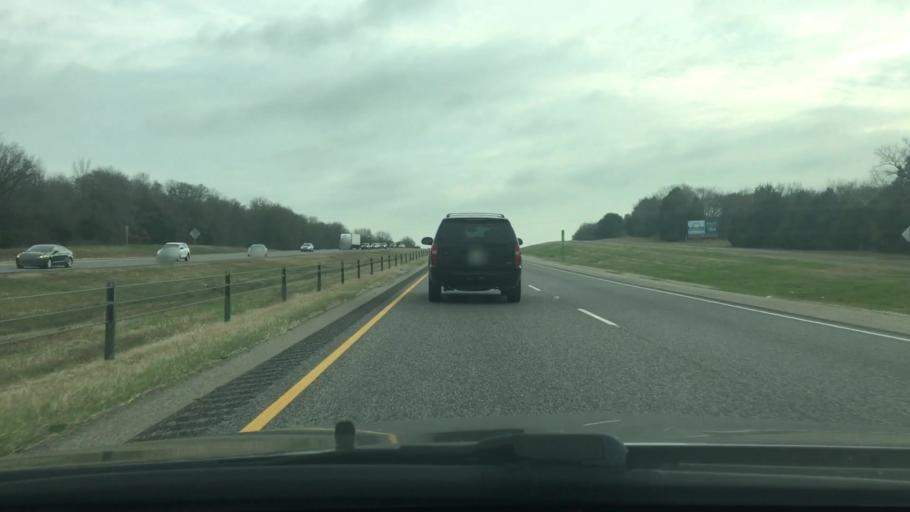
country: US
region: Texas
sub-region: Freestone County
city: Fairfield
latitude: 31.6440
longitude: -96.1591
